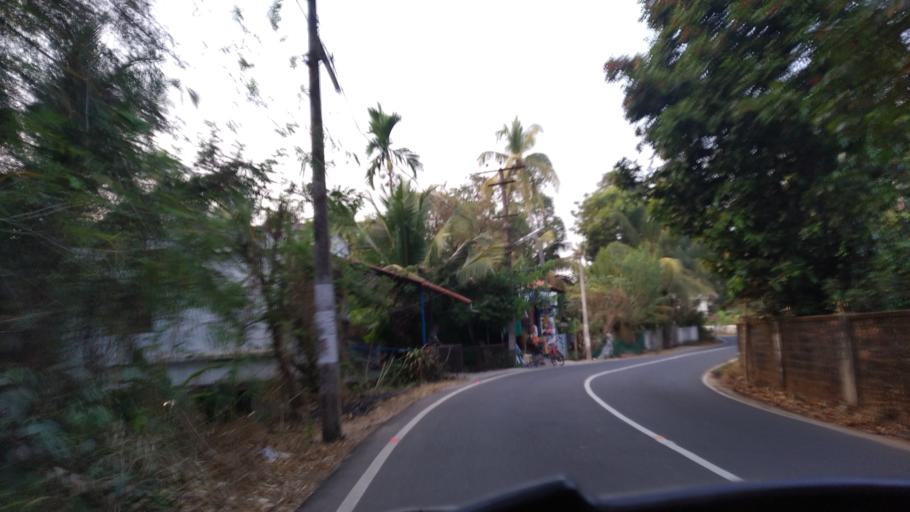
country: IN
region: Kerala
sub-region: Ernakulam
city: Elur
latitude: 10.1114
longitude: 76.2439
